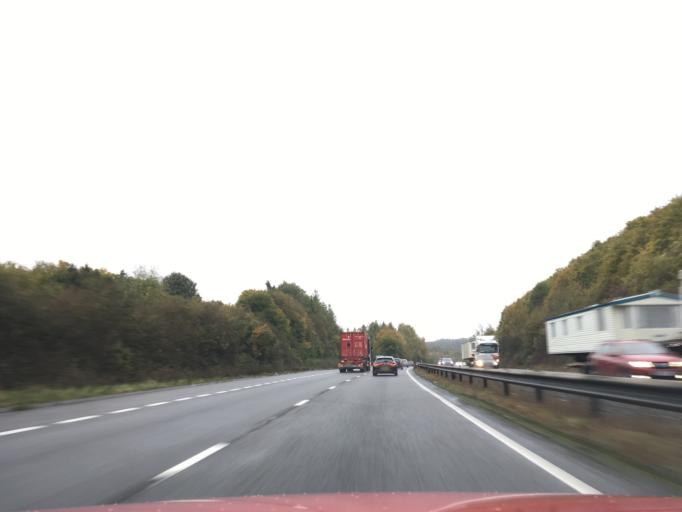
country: GB
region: England
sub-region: Hampshire
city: Highclere
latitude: 51.2819
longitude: -1.3413
